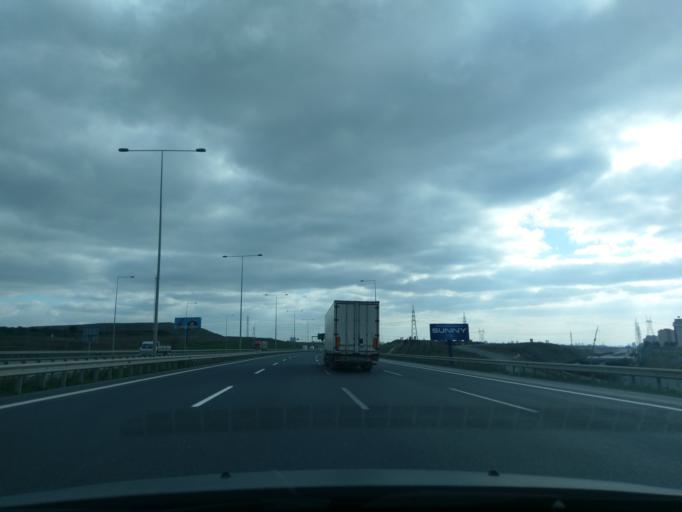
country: TR
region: Istanbul
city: Basaksehir
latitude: 41.1242
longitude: 28.8110
